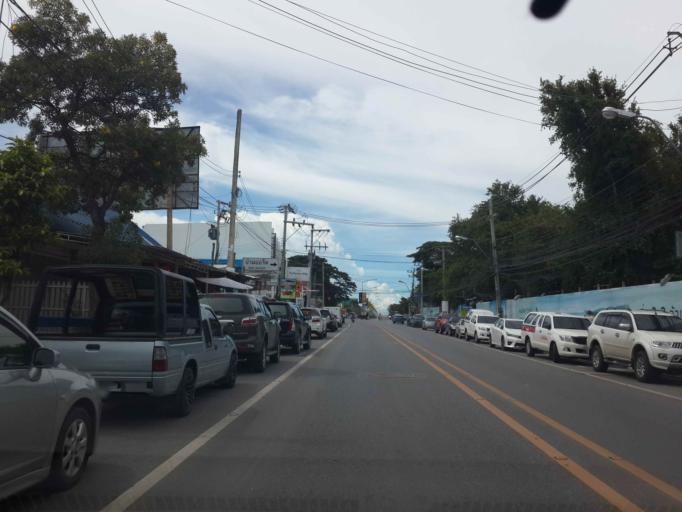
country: TH
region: Prachuap Khiri Khan
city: Hua Hin
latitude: 12.5324
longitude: 99.9659
